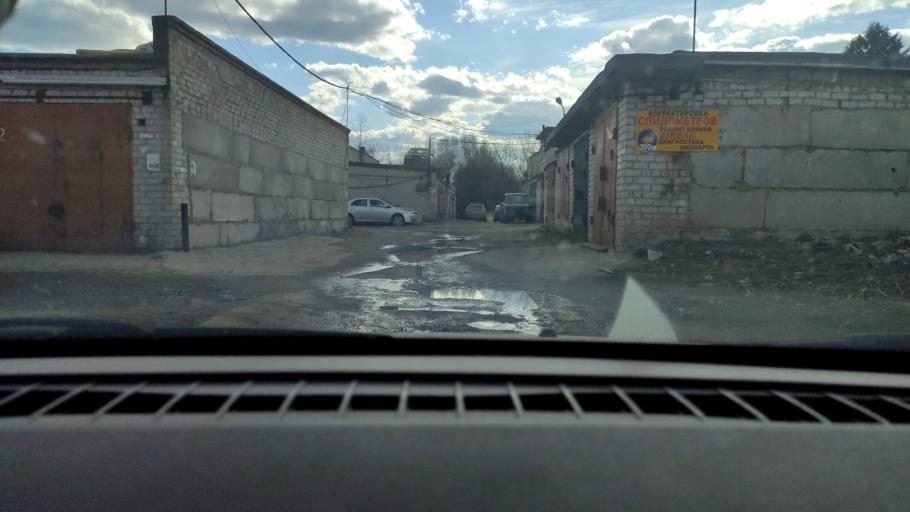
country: RU
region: Perm
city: Perm
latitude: 57.9573
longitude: 56.1993
